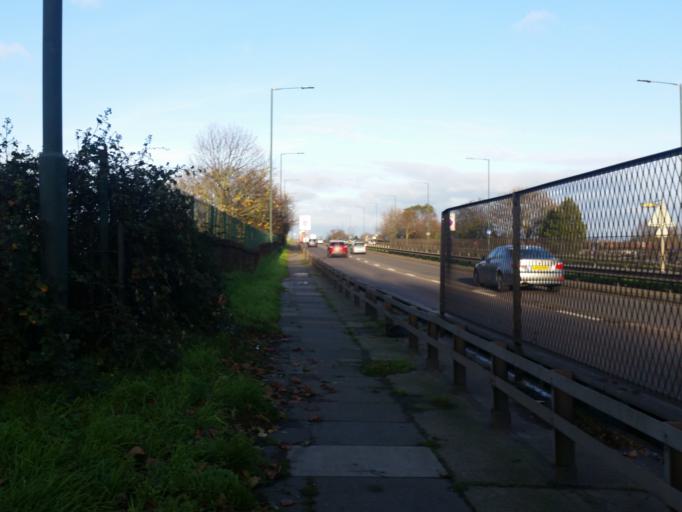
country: GB
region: England
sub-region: Greater London
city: Enfield
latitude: 51.6357
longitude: -0.0684
